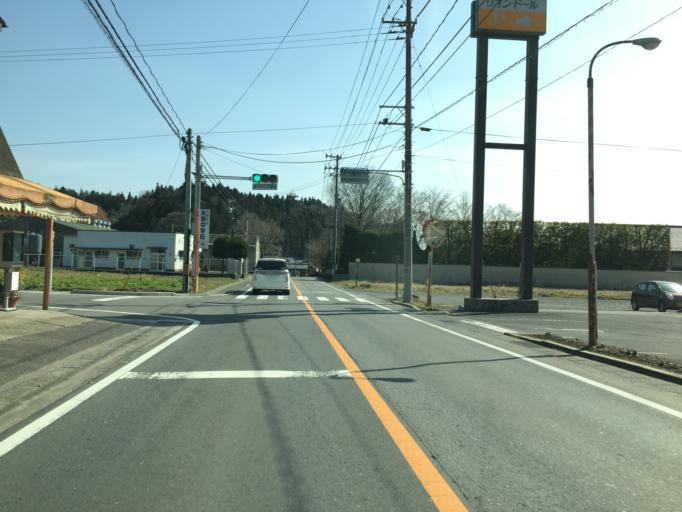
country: JP
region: Ibaraki
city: Daigo
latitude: 36.8782
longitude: 140.4226
